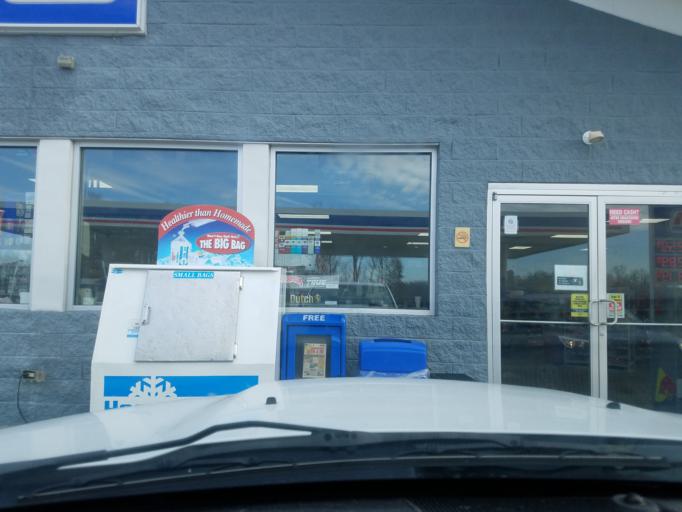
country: US
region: Indiana
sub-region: Crawford County
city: English
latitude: 38.2241
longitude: -86.5901
